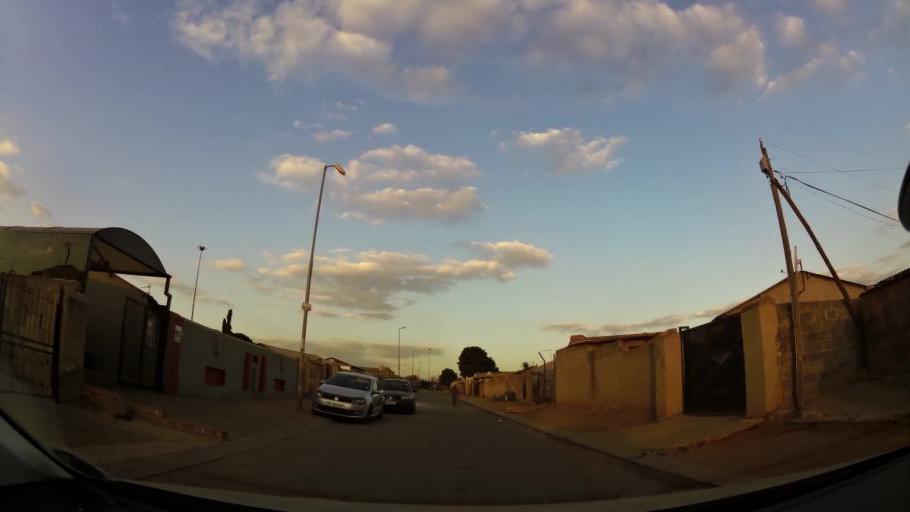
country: ZA
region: Gauteng
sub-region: City of Johannesburg Metropolitan Municipality
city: Soweto
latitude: -26.2747
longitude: 27.8959
